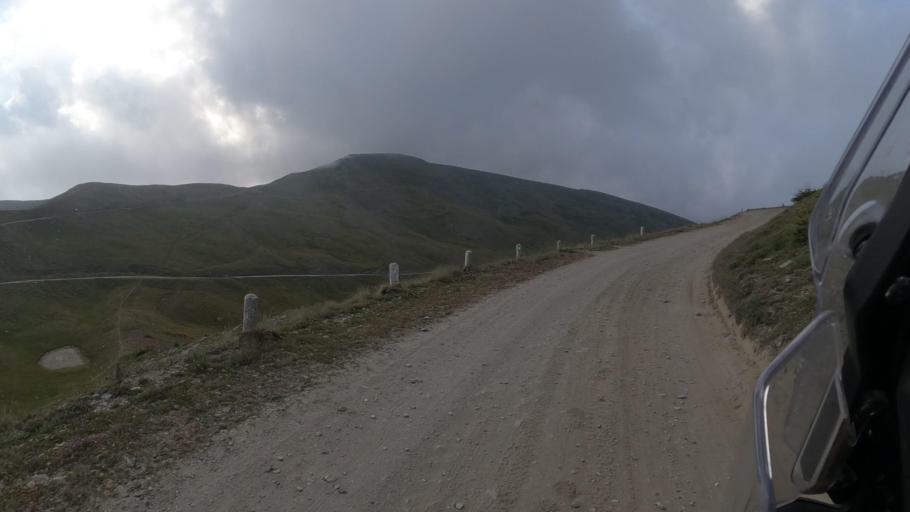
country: IT
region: Piedmont
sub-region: Provincia di Torino
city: Exilles
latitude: 45.0697
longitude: 6.9568
